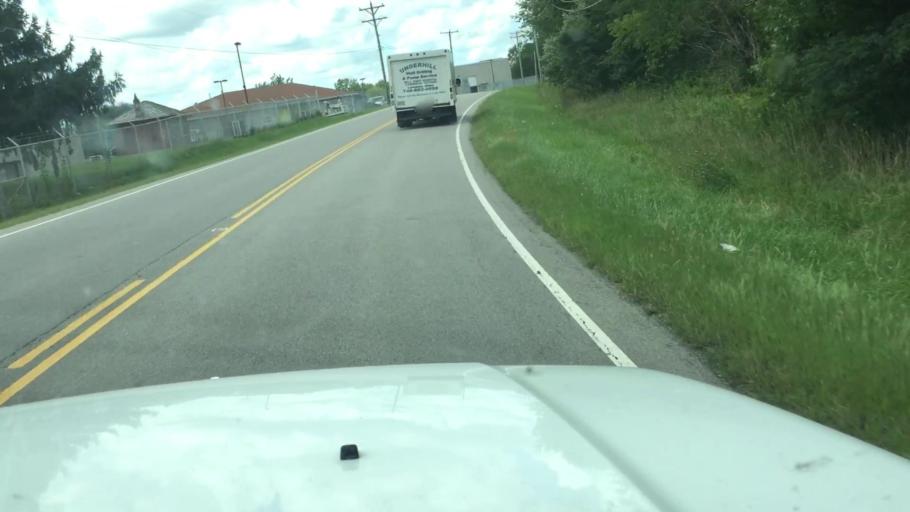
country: US
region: Ohio
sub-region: Madison County
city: London
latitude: 39.8762
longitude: -83.4331
